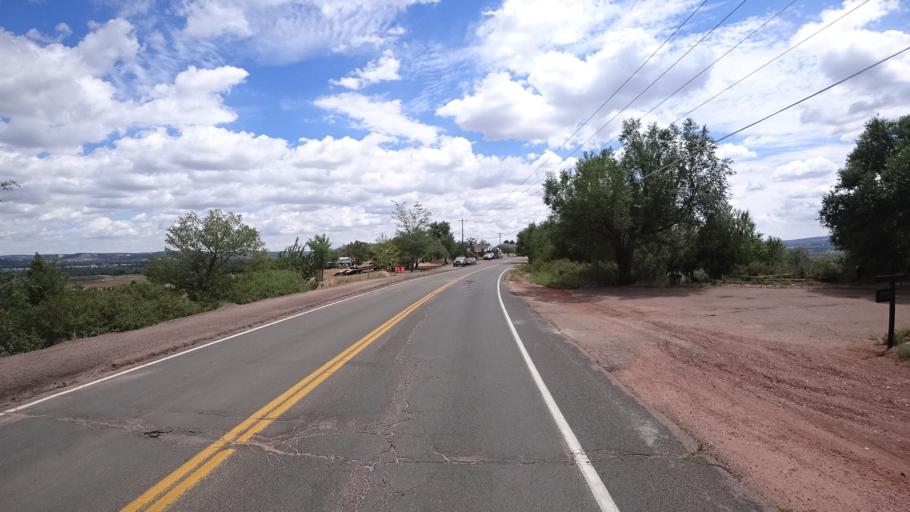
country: US
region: Colorado
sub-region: El Paso County
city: Colorado Springs
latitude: 38.8633
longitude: -104.8518
